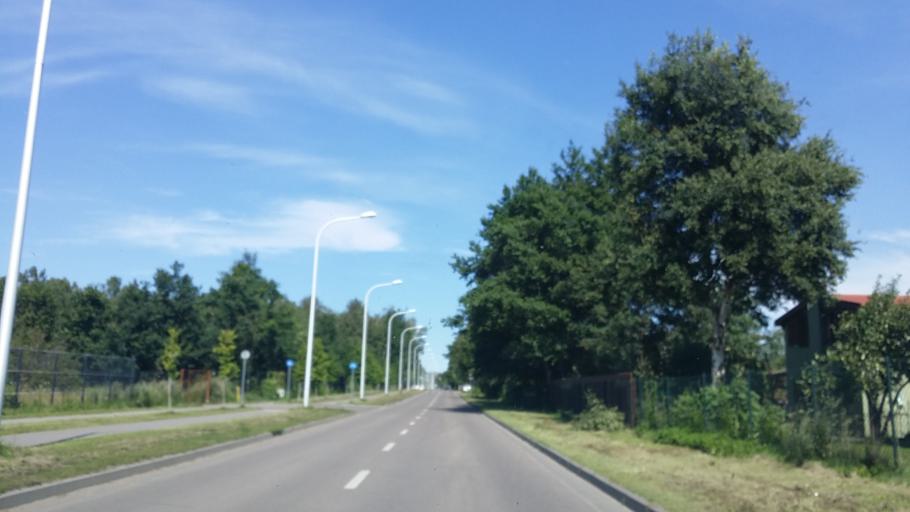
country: PL
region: West Pomeranian Voivodeship
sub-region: Powiat kolobrzeski
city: Grzybowo
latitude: 54.1702
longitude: 15.5308
